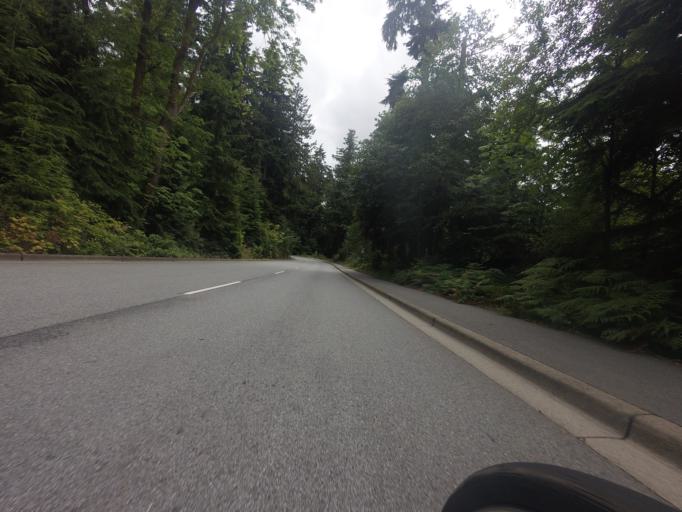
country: CA
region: British Columbia
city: West End
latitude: 49.3087
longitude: -123.1523
